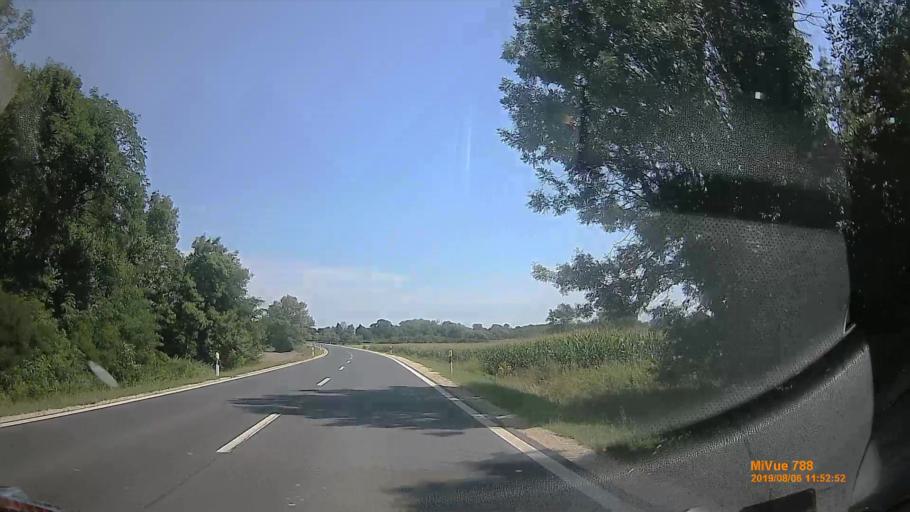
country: HU
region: Vas
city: Kormend
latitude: 47.0379
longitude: 16.6596
